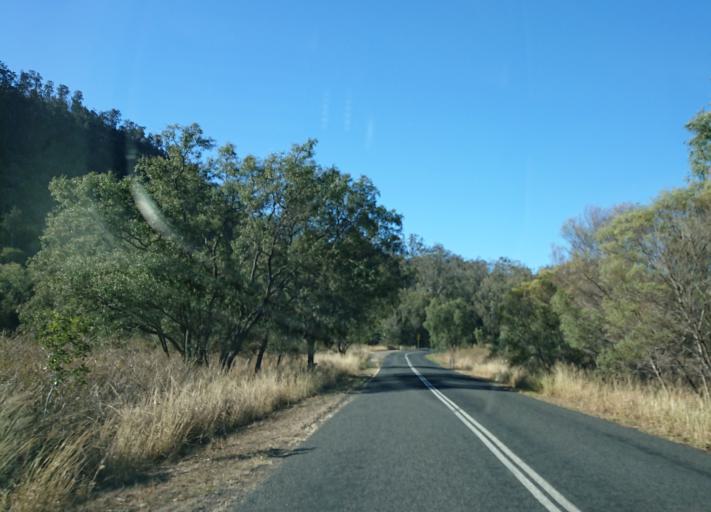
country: AU
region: Queensland
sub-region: Toowoomba
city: Top Camp
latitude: -27.7390
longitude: 152.0991
